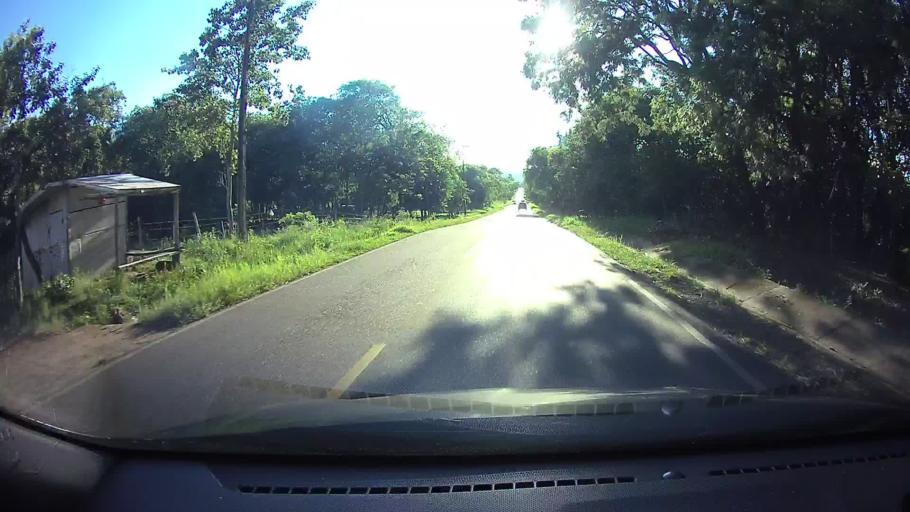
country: PY
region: Cordillera
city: Emboscada
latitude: -25.2021
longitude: -57.3300
